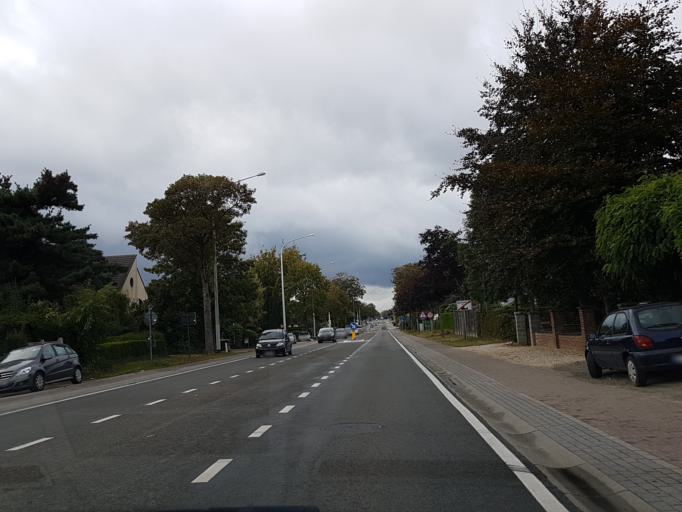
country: BE
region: Flanders
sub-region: Provincie Vlaams-Brabant
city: Bierbeek
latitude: 50.8632
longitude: 4.7595
